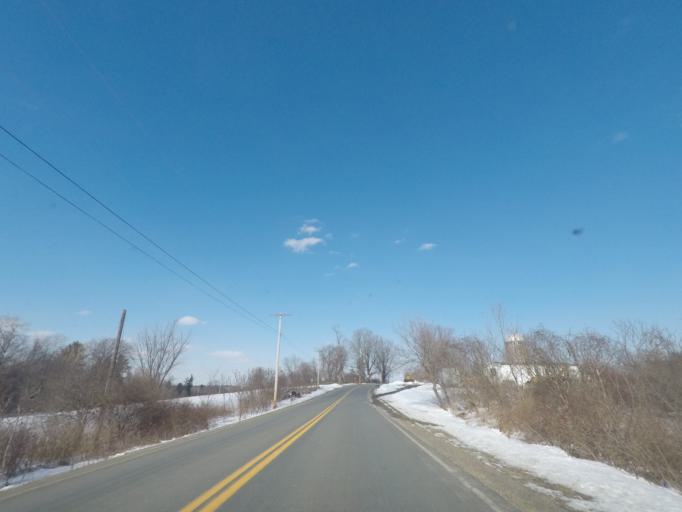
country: US
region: New York
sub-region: Saratoga County
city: Stillwater
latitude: 42.8654
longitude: -73.5943
